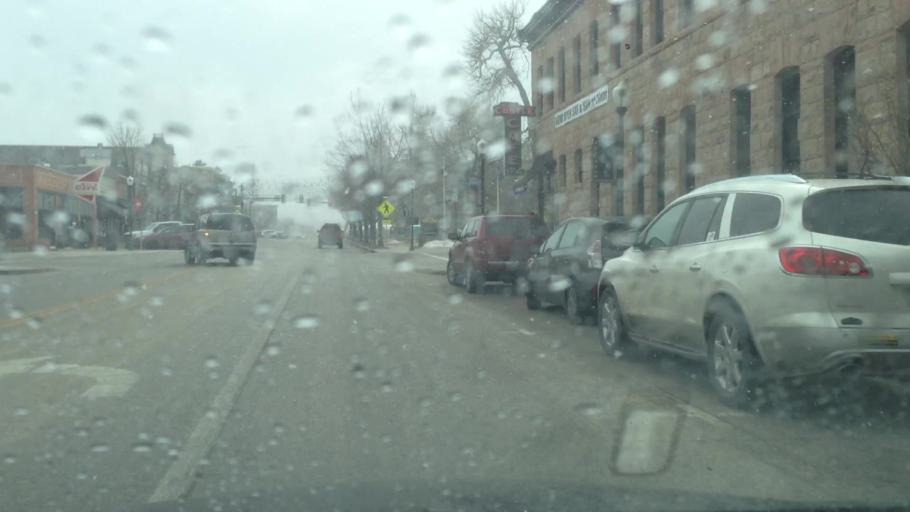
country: US
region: Colorado
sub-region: Douglas County
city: Castle Rock
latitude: 39.3739
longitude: -104.8600
